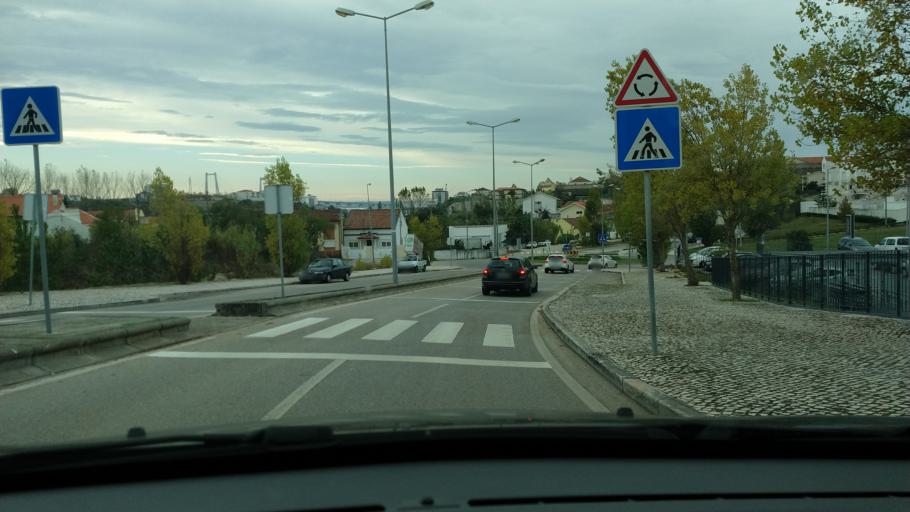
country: PT
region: Coimbra
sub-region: Figueira da Foz
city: Tavarede
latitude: 40.1577
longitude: -8.8495
